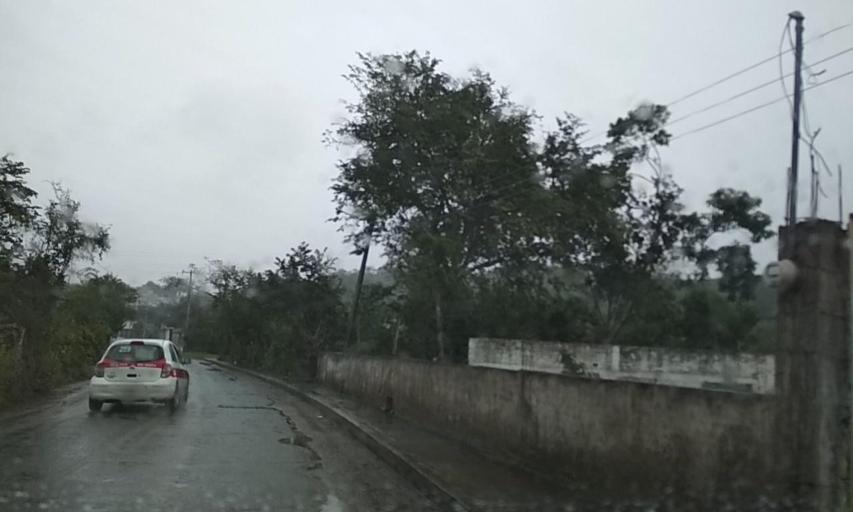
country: MX
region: Veracruz
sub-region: Papantla
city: El Chote
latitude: 20.4007
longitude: -97.3429
